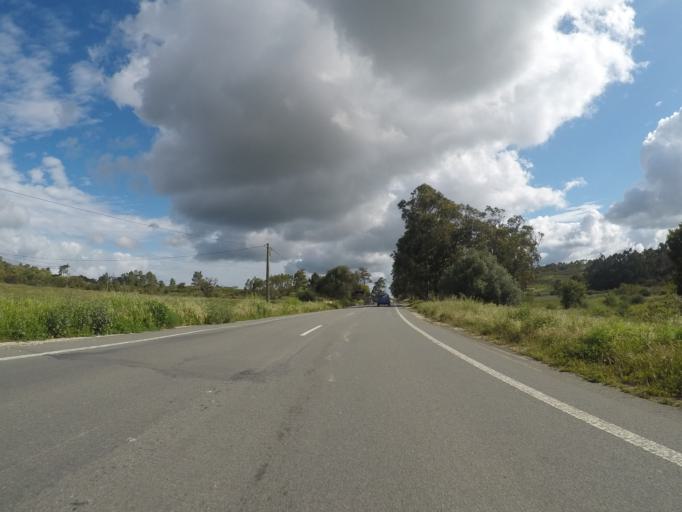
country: PT
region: Faro
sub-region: Aljezur
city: Aljezur
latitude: 37.2987
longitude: -8.8001
